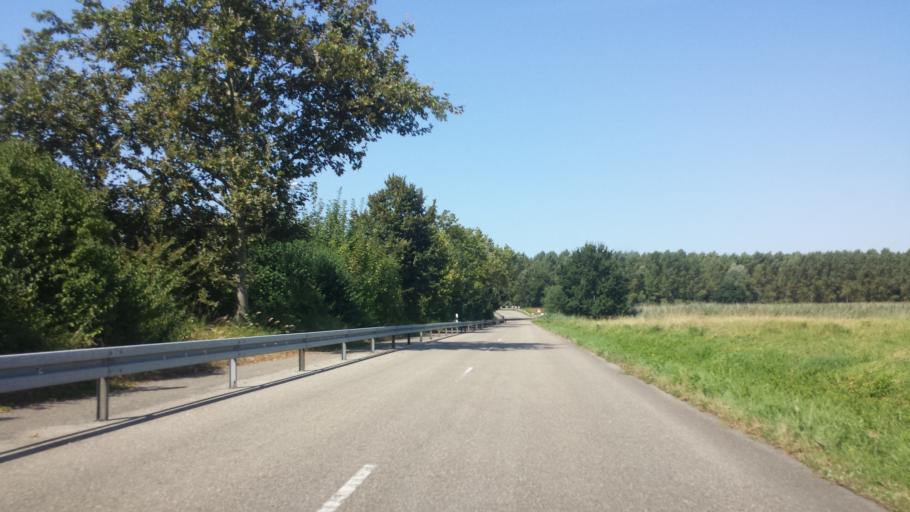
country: DE
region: Baden-Wuerttemberg
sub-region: Karlsruhe Region
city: Philippsburg
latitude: 49.2554
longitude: 8.4417
